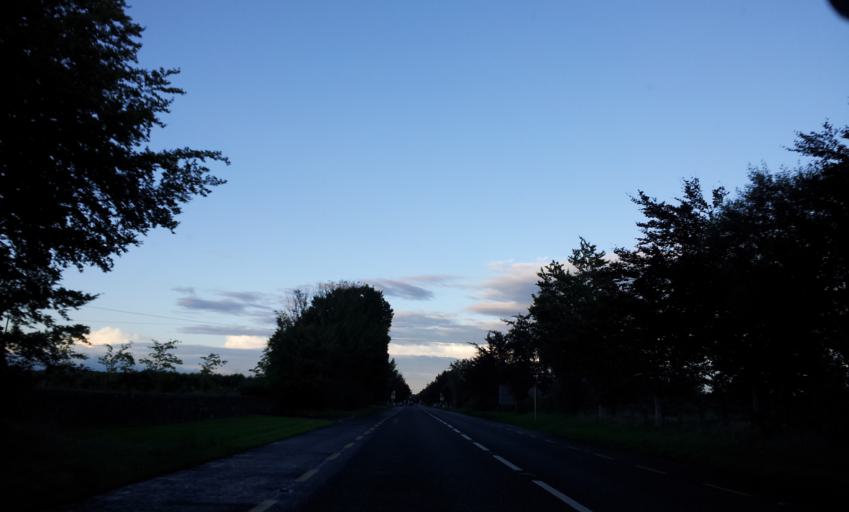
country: IE
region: Munster
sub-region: County Limerick
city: Newcastle West
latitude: 52.4404
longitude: -9.0843
